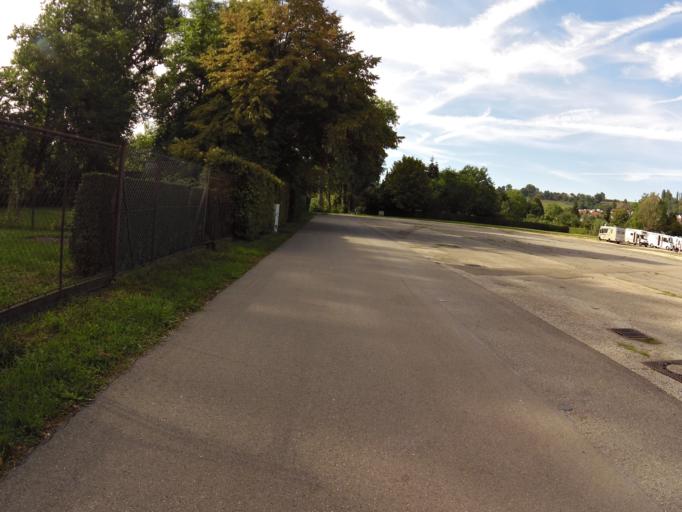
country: DE
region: Baden-Wuerttemberg
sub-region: Regierungsbezirk Stuttgart
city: Nurtingen
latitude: 48.6364
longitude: 9.3322
